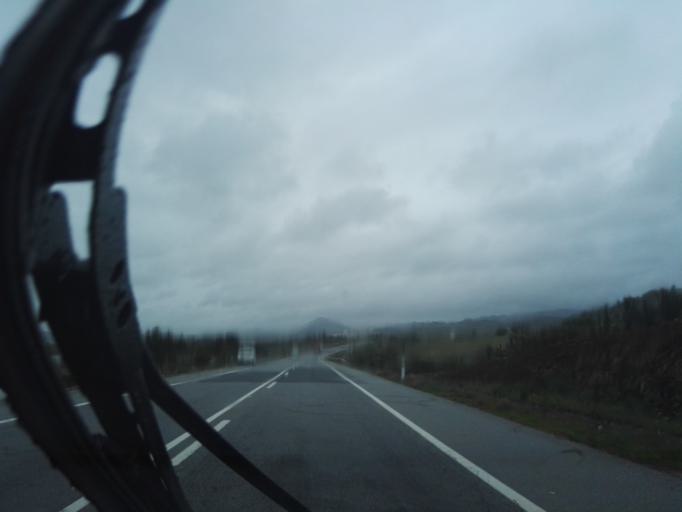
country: PT
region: Portalegre
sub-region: Portalegre
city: Urra
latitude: 39.2499
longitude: -7.4039
